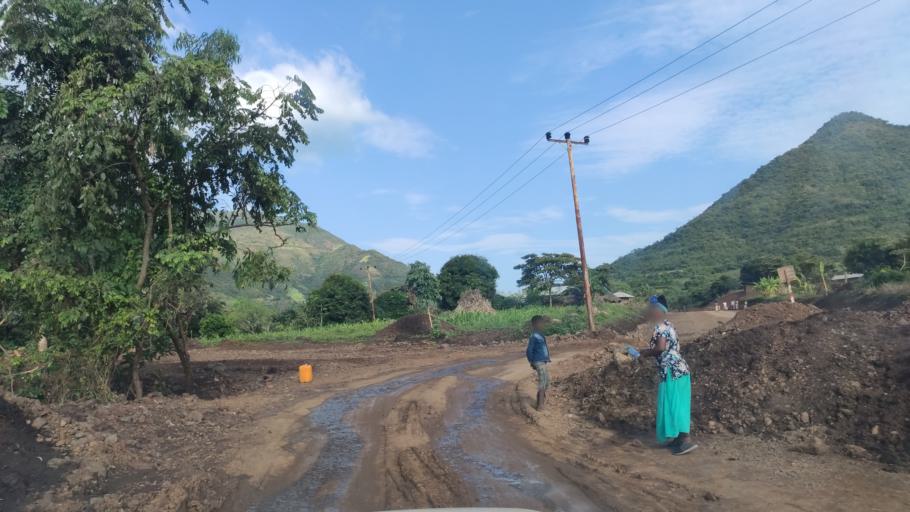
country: ET
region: Southern Nations, Nationalities, and People's Region
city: Arba Minch'
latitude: 6.4260
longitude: 37.3340
